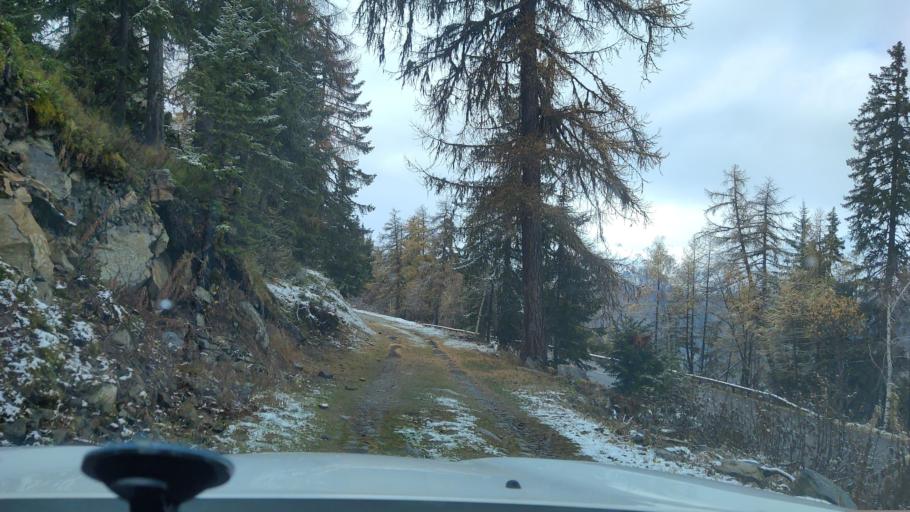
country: FR
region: Rhone-Alpes
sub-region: Departement de la Savoie
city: Seez
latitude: 45.5991
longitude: 6.8153
